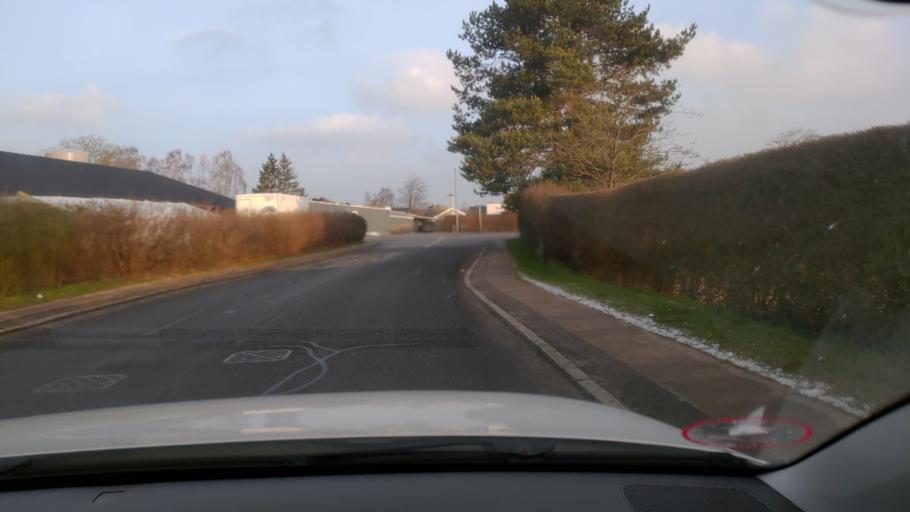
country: DK
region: Zealand
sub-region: Solrod Kommune
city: Solrod Strand
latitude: 55.5381
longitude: 12.2135
